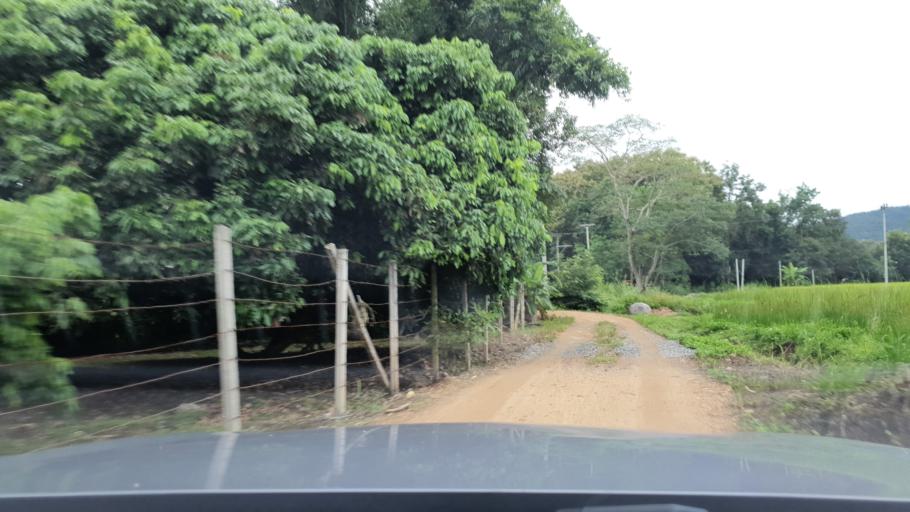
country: TH
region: Chiang Mai
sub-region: Amphoe Chiang Dao
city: Chiang Dao
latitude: 19.3307
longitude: 98.9353
